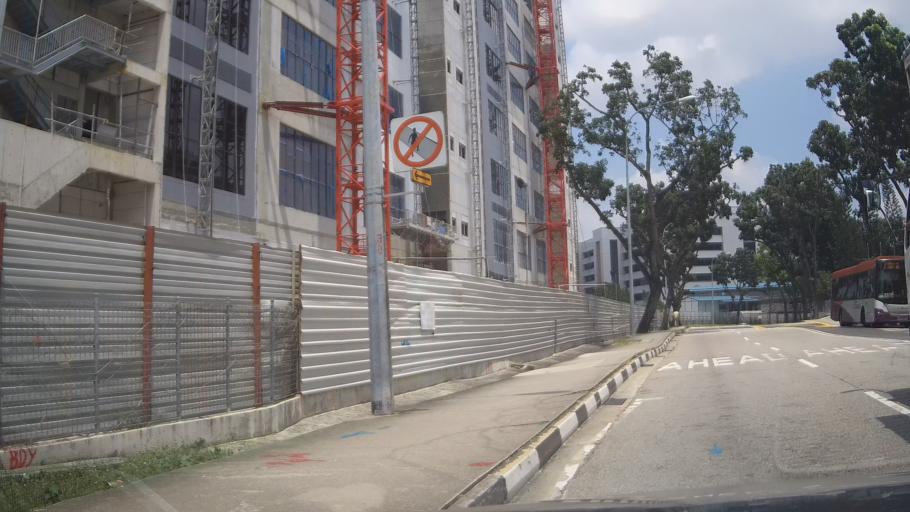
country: SG
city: Singapore
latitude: 1.3240
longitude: 103.8746
